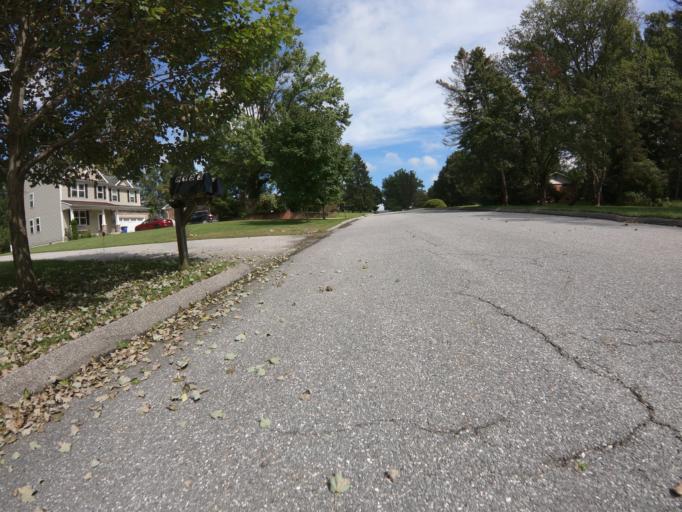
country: US
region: Maryland
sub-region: Howard County
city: Ellicott City
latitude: 39.3006
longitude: -76.8232
